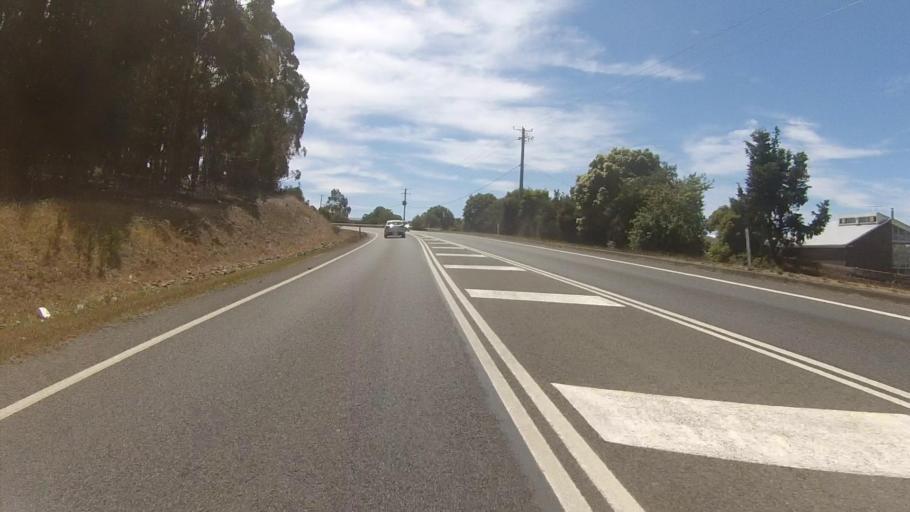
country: AU
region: Tasmania
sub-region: Kingborough
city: Margate
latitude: -43.0045
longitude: 147.2748
